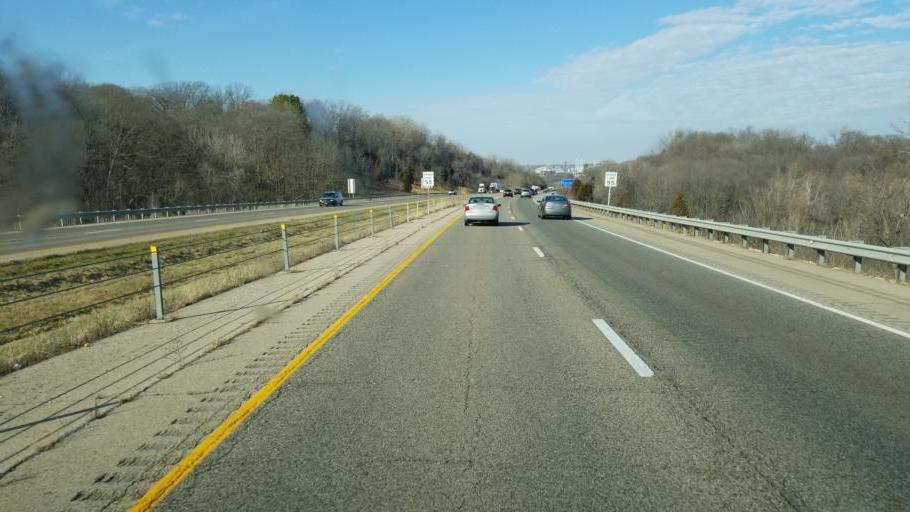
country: US
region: Illinois
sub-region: Tazewell County
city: East Peoria
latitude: 40.6530
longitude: -89.5606
